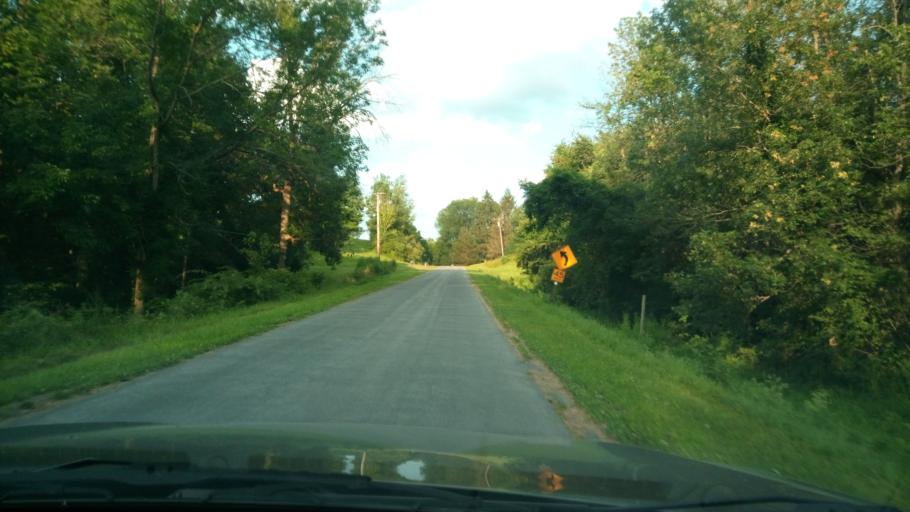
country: US
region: New York
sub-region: Wayne County
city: Clyde
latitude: 43.0792
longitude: -76.9291
